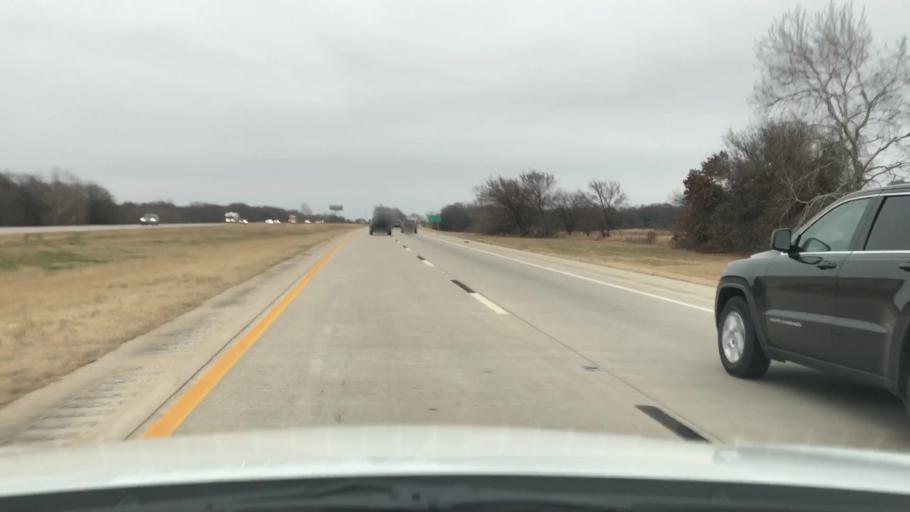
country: US
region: Oklahoma
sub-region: Love County
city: Marietta
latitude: 33.8043
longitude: -97.1348
